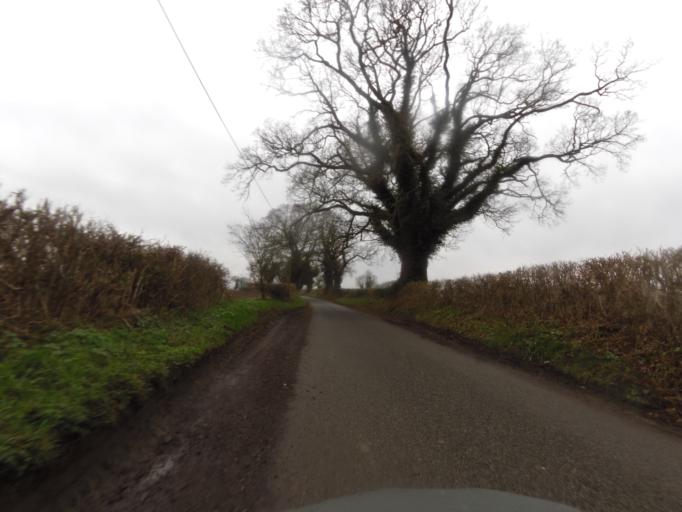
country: GB
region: England
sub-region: Norfolk
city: Briston
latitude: 52.8126
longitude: 1.0883
